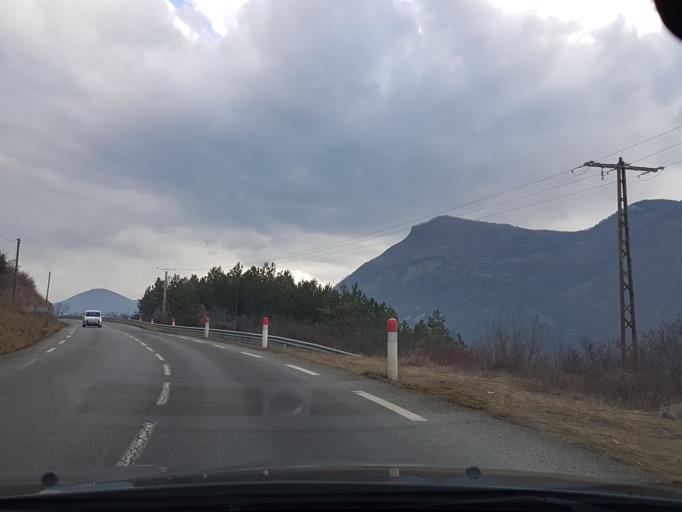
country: FR
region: Provence-Alpes-Cote d'Azur
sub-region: Departement des Hautes-Alpes
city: Tallard
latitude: 44.4681
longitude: 6.1360
